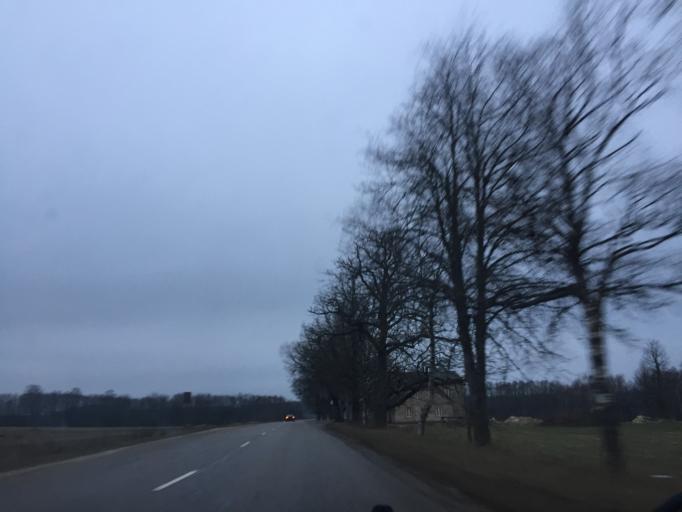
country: LV
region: Priekuli
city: Priekuli
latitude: 57.3242
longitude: 25.4536
